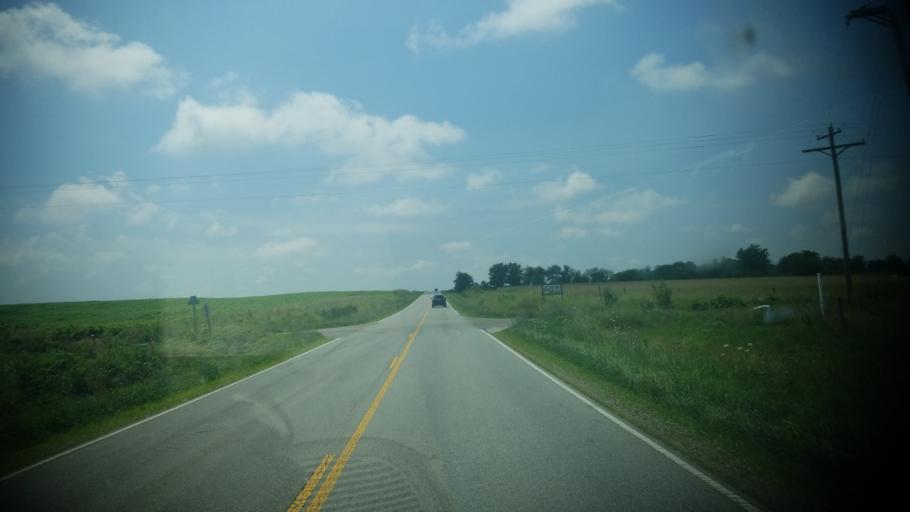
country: US
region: Illinois
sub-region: Wayne County
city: Fairfield
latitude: 38.4304
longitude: -88.3496
